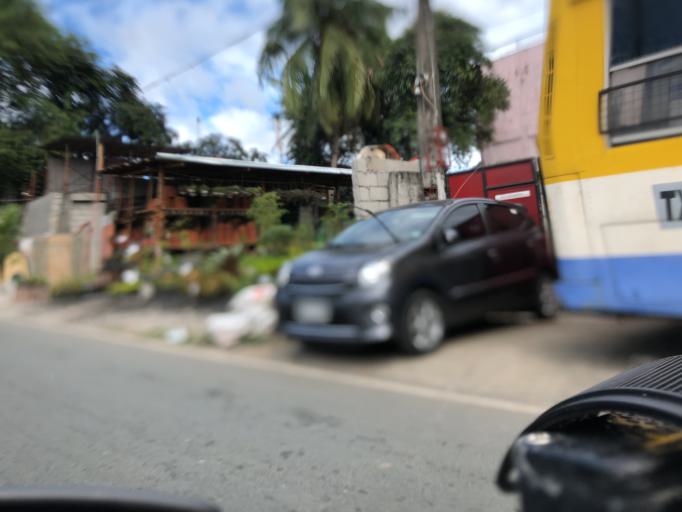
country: PH
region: Central Luzon
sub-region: Province of Bulacan
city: San Jose del Monte
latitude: 14.7456
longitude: 121.0533
